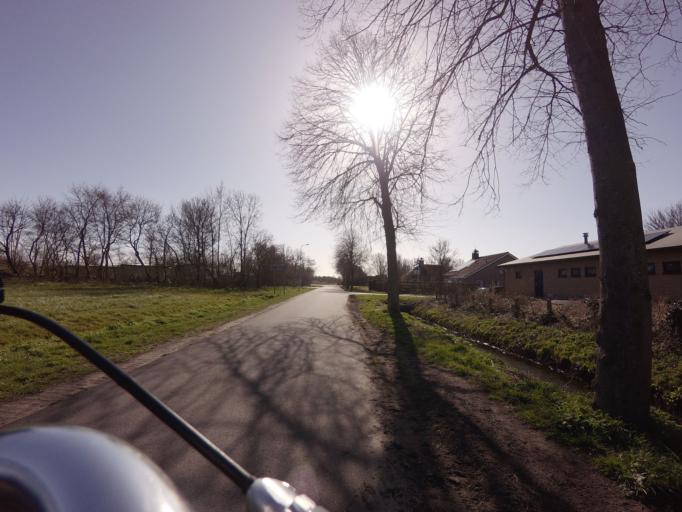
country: NL
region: Zeeland
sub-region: Schouwen-Duiveland
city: Renesse
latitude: 51.7315
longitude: 3.7814
